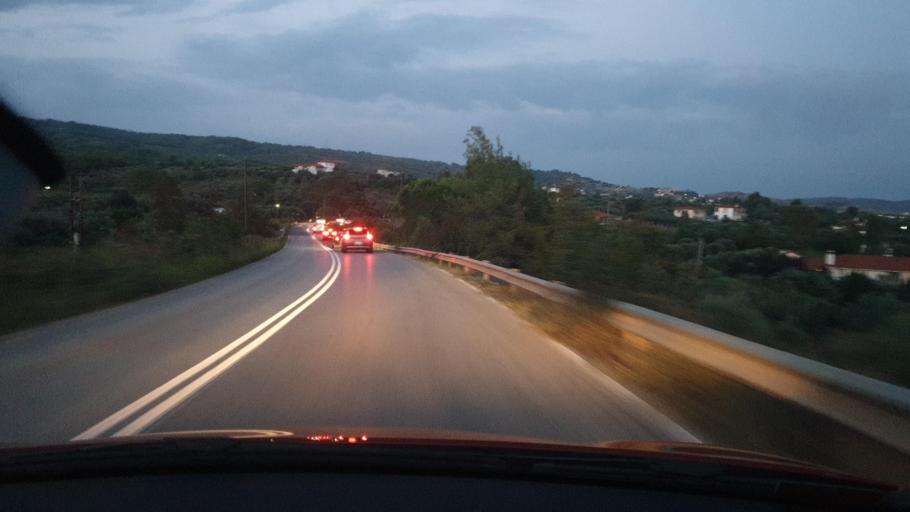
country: GR
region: Central Macedonia
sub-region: Nomos Chalkidikis
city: Nikiti
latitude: 40.2269
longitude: 23.6436
